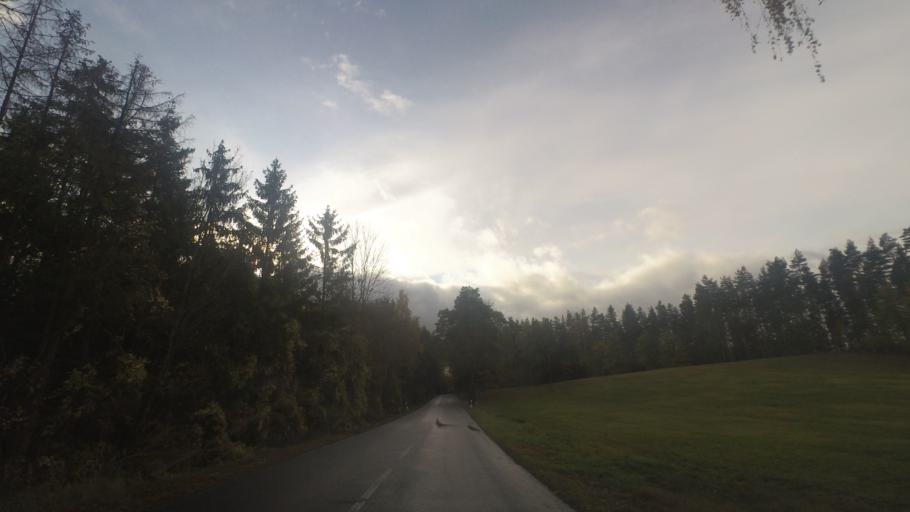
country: DE
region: Thuringia
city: Saalfeld
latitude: 50.6850
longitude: 11.3807
